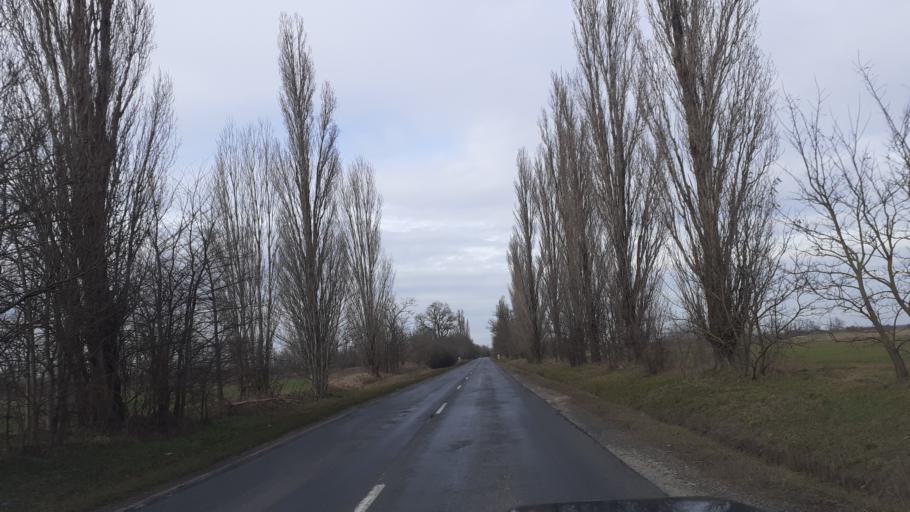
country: HU
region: Fejer
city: Soponya
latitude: 47.0576
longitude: 18.4206
